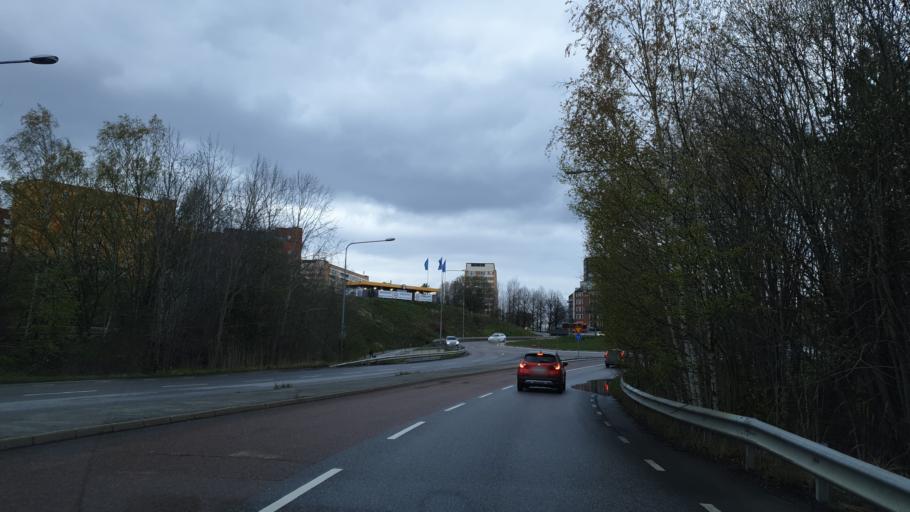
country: SE
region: Stockholm
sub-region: Solna Kommun
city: Solna
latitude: 59.3487
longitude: 18.0068
